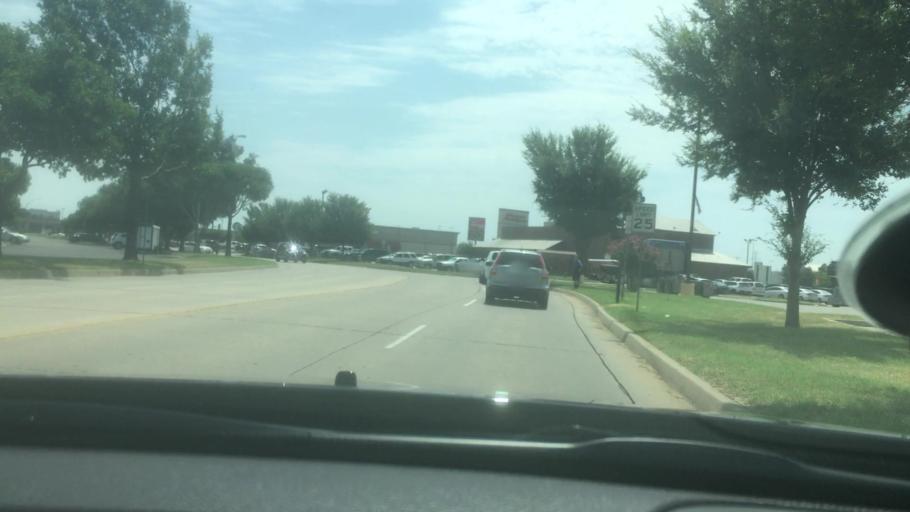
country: US
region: Oklahoma
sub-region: Oklahoma County
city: Bethany
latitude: 35.4616
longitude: -97.6245
